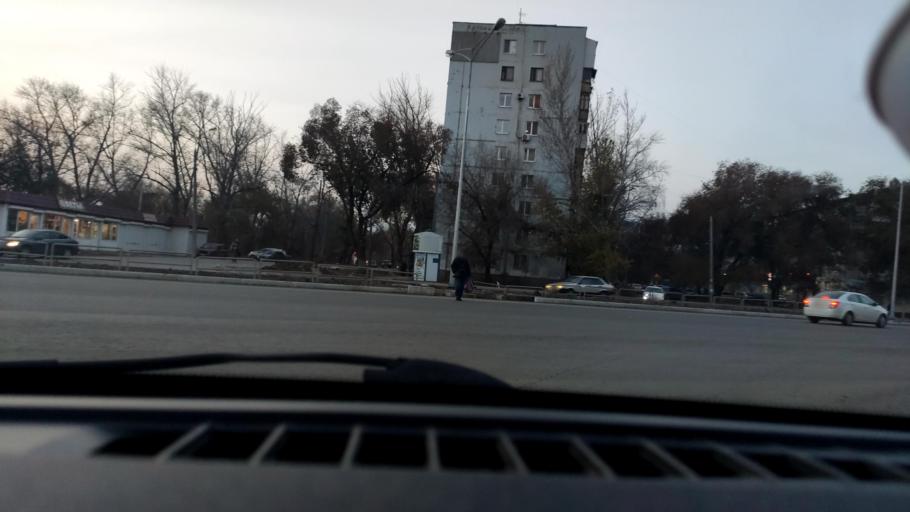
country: RU
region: Samara
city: Samara
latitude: 53.1074
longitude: 50.0804
